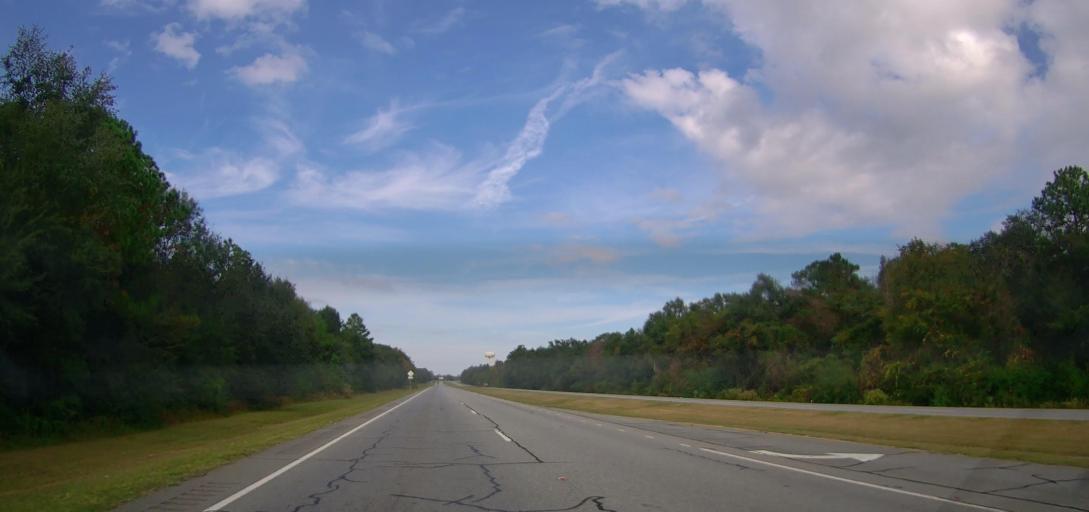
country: US
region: Georgia
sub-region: Mitchell County
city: Camilla
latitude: 31.2617
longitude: -84.1951
